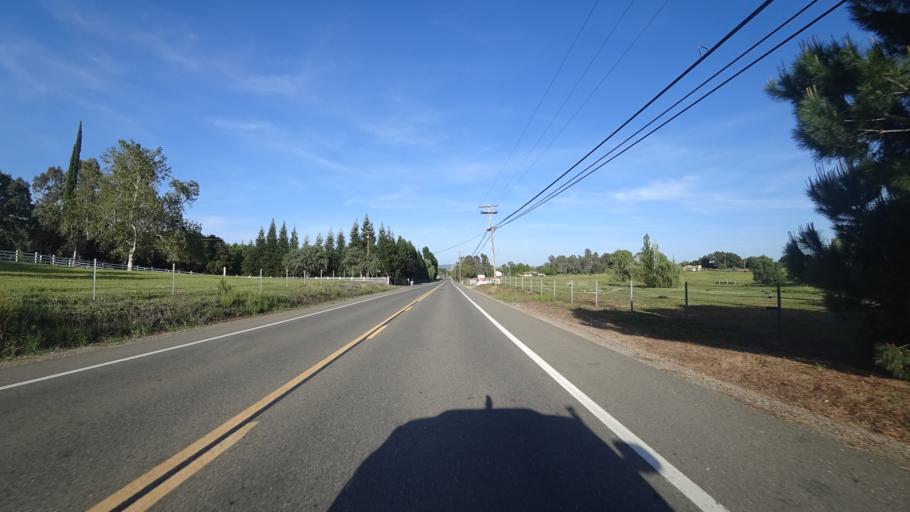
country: US
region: California
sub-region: Placer County
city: Lincoln
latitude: 38.9265
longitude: -121.2541
